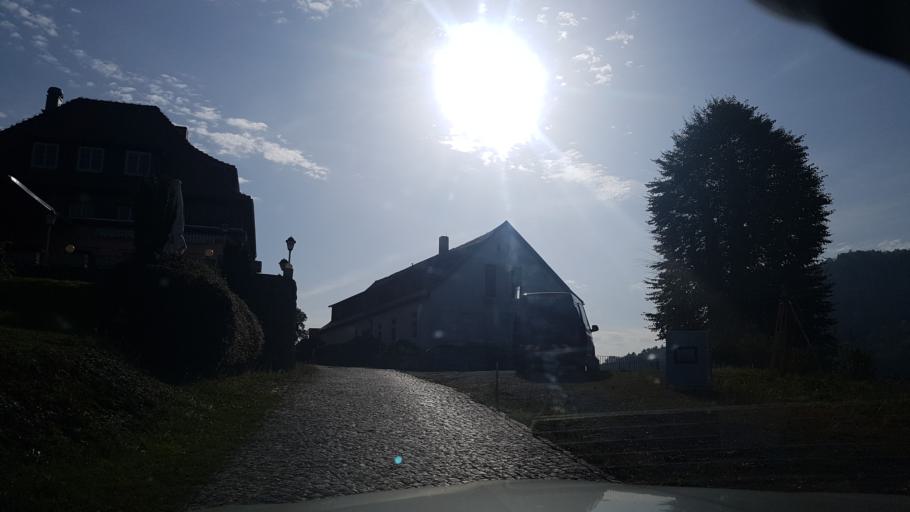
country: DE
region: Saxony
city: Konigstein
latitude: 50.9072
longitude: 14.0840
